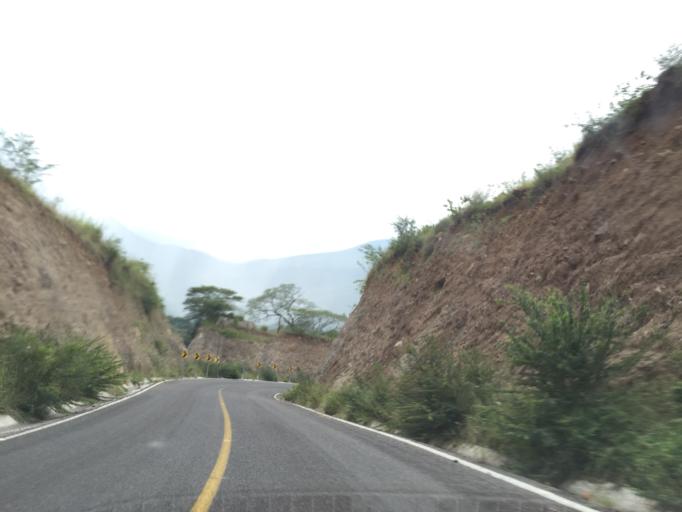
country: MX
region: Colima
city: Comala
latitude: 19.3672
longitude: -103.7990
